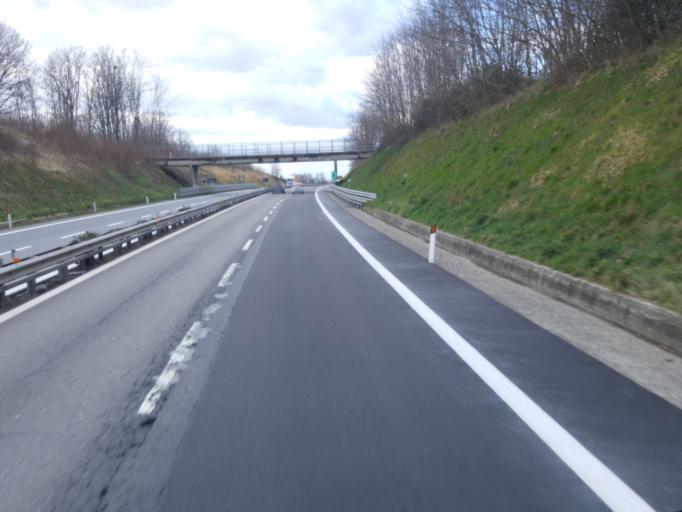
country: IT
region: Calabria
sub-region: Provincia di Cosenza
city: Piane Crati
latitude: 39.2156
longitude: 16.3058
